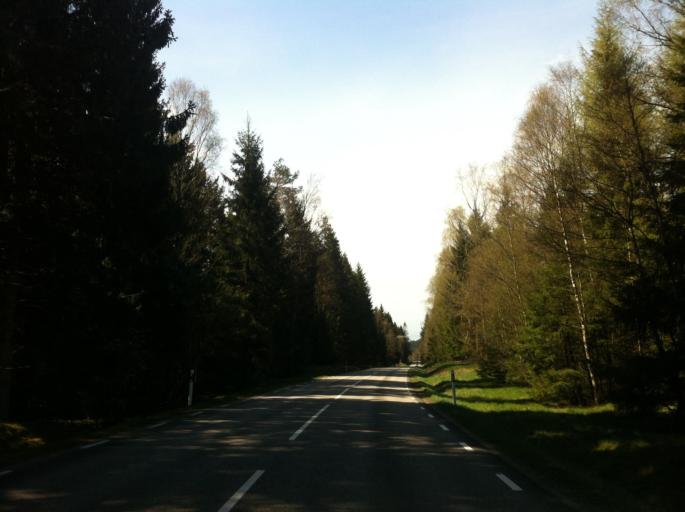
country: SE
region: Vaestra Goetaland
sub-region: Marks Kommun
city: Kinna
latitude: 57.1879
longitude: 12.7910
